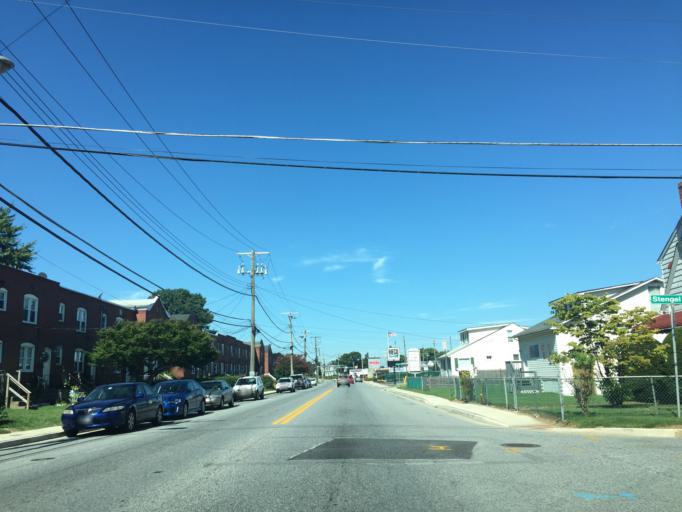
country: US
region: Maryland
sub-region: Baltimore County
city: Dundalk
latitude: 39.2725
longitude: -76.5148
